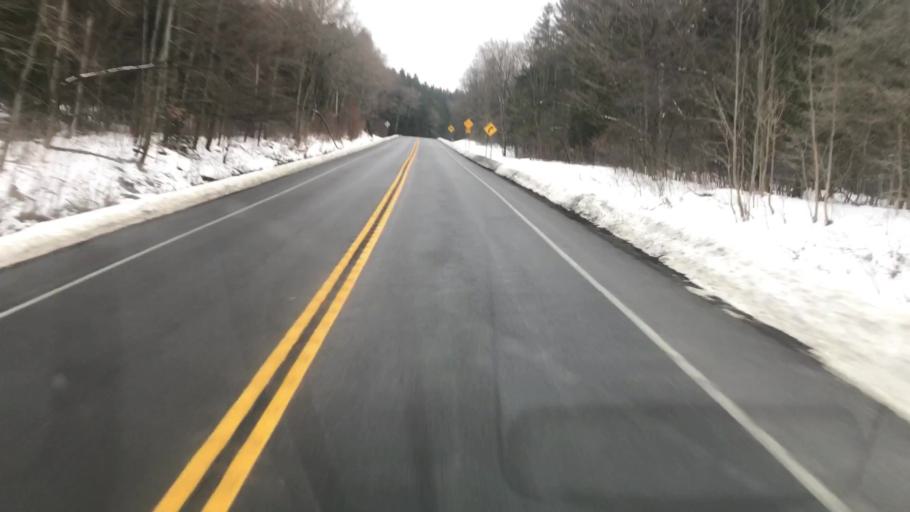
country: US
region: New York
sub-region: Cayuga County
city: Moravia
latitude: 42.7492
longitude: -76.3260
